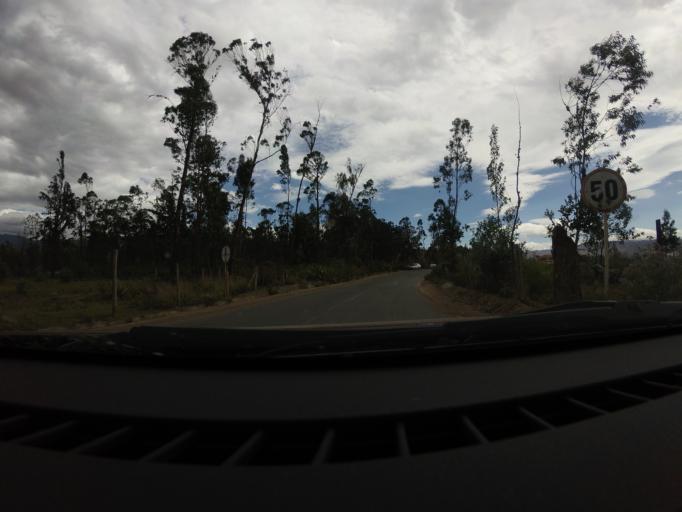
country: CO
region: Boyaca
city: Villa de Leiva
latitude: 5.6339
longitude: -73.5588
